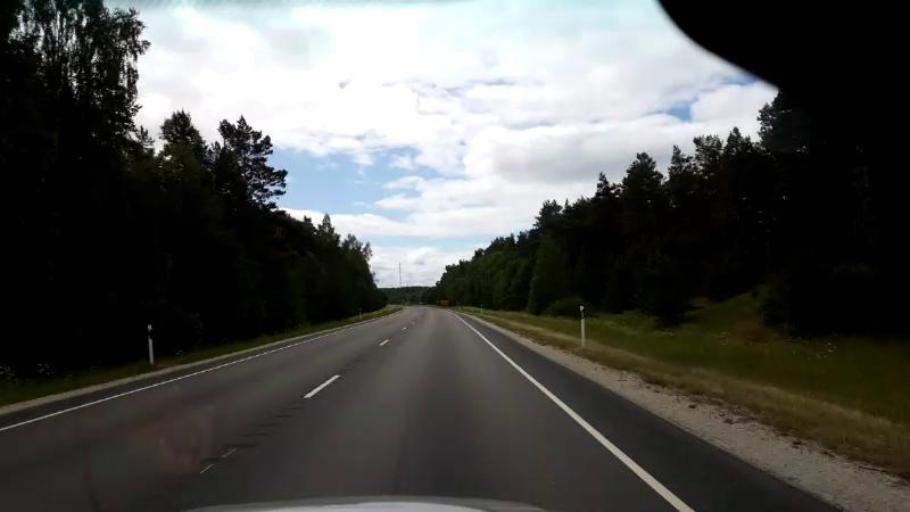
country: LV
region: Salacgrivas
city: Ainazi
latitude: 58.0893
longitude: 24.5080
